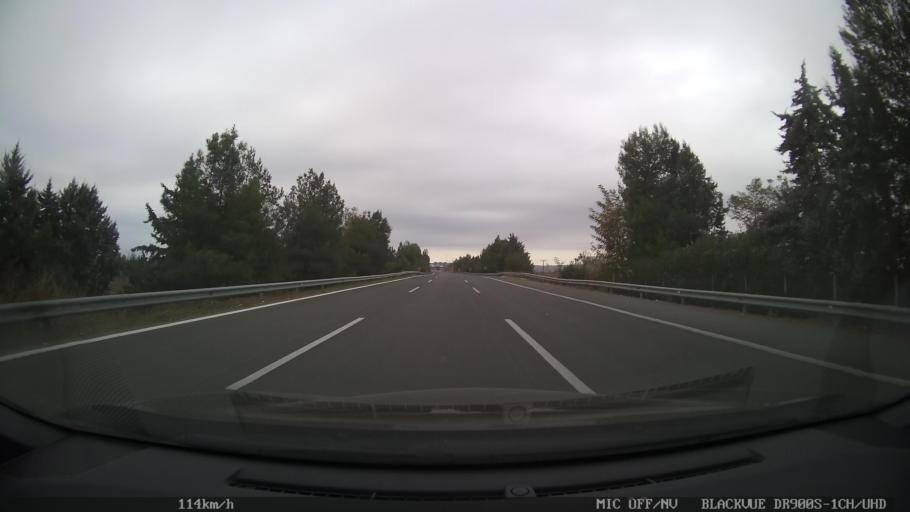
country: GR
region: Central Macedonia
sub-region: Nomos Imathias
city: Kleidi
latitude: 40.5270
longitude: 22.5751
